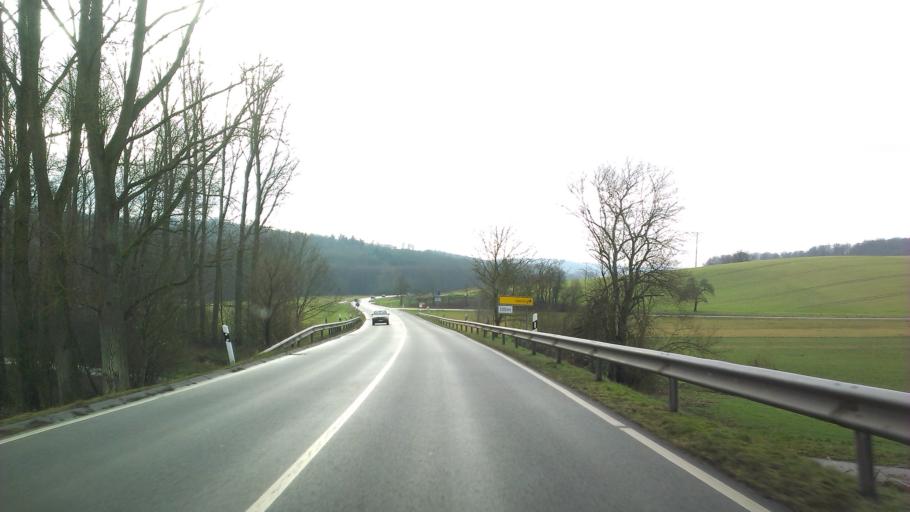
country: DE
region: Baden-Wuerttemberg
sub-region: Karlsruhe Region
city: Horrenberg
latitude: 49.3058
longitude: 8.7870
